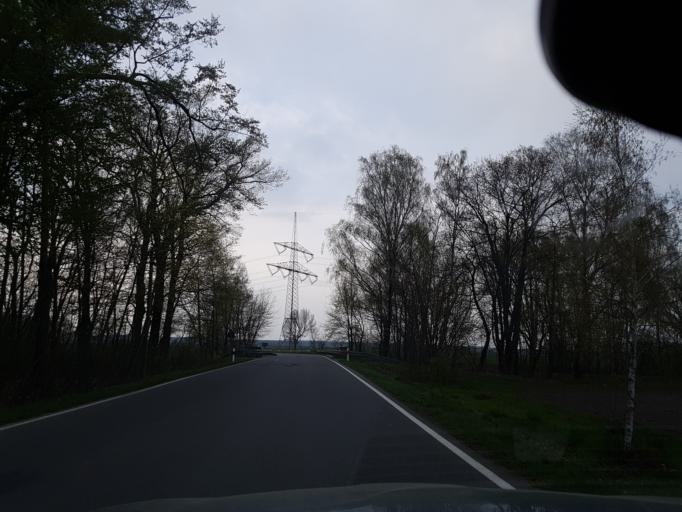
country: DE
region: Brandenburg
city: Schraden
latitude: 51.4485
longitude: 13.6731
